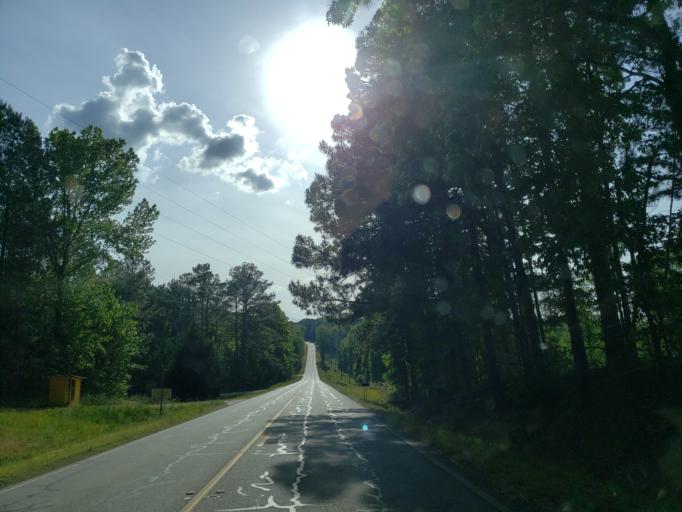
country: US
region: Georgia
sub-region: Carroll County
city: Bowdon
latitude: 33.4734
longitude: -85.2730
